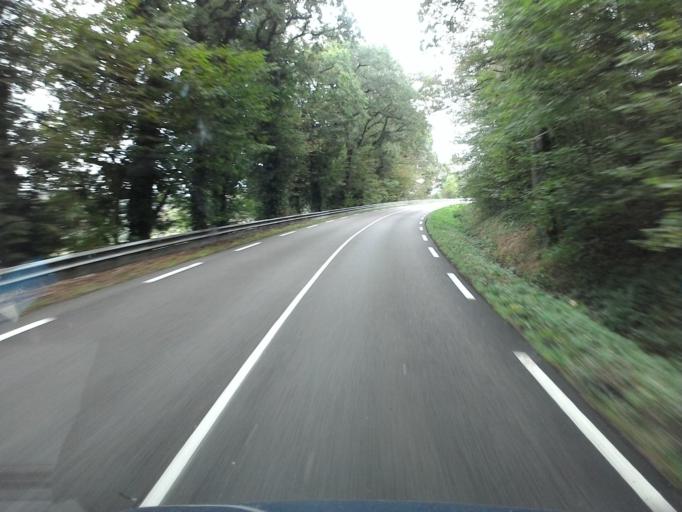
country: FR
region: Bourgogne
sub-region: Departement de Saone-et-Loire
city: Saint-Vallier
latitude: 46.6498
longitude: 4.4364
